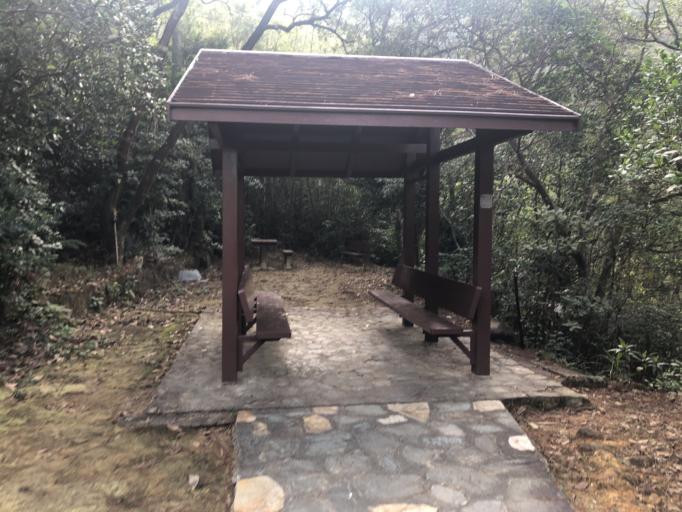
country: HK
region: Wanchai
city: Wan Chai
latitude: 22.2711
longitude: 114.2106
